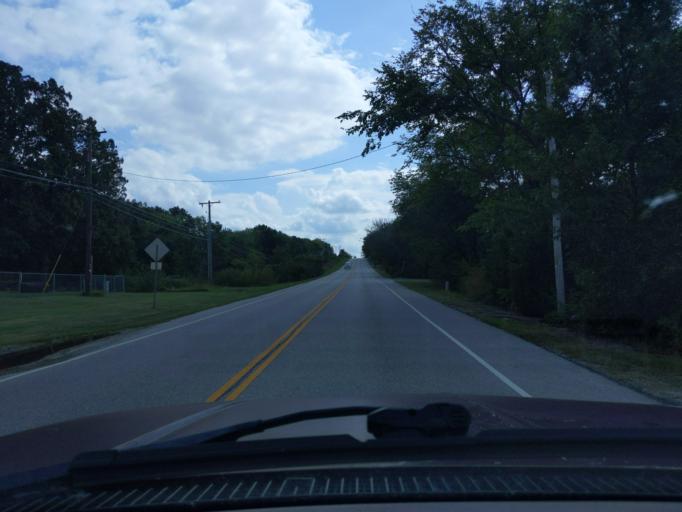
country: US
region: Oklahoma
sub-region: Tulsa County
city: Oakhurst
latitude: 36.0582
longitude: -96.0117
